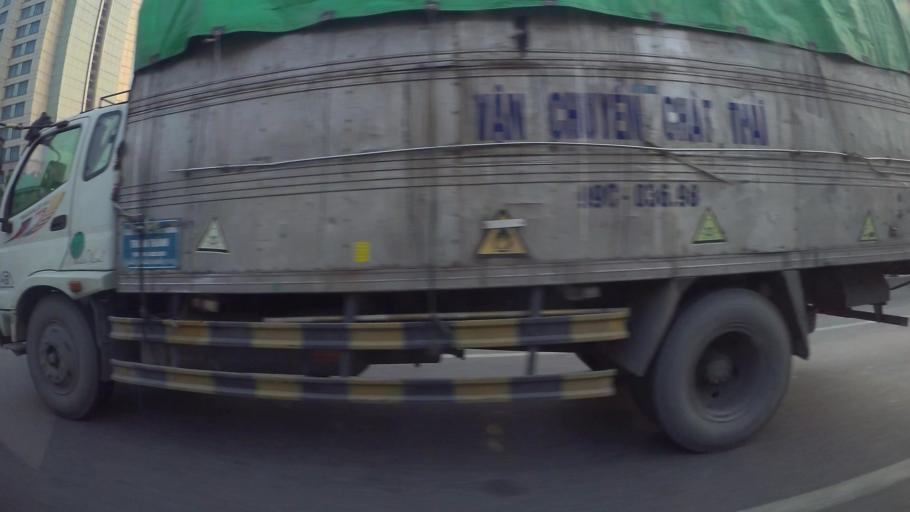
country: VN
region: Ha Noi
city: Van Dien
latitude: 20.9702
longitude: 105.8265
